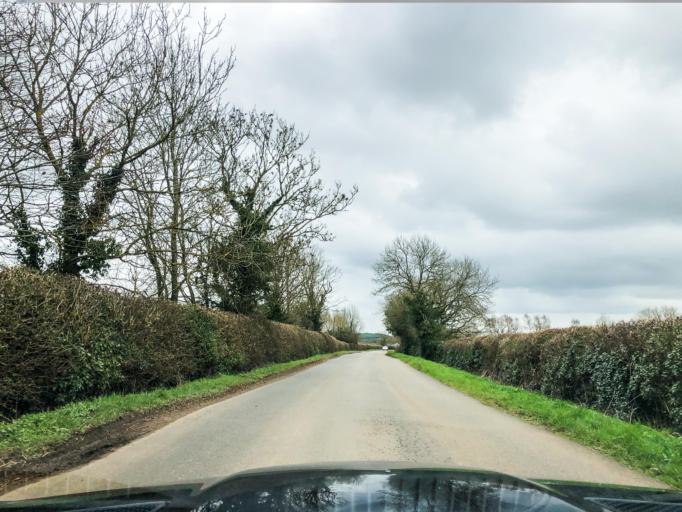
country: GB
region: England
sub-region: Oxfordshire
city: Hook Norton
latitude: 52.0829
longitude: -1.4788
